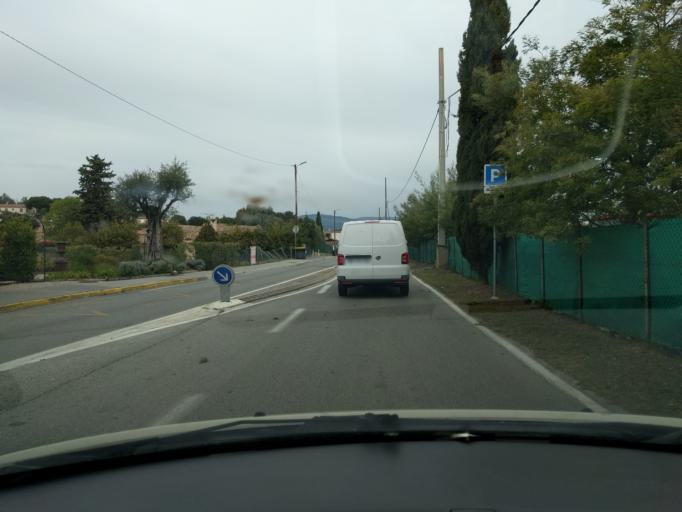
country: FR
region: Provence-Alpes-Cote d'Azur
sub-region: Departement des Alpes-Maritimes
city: La Roquette-sur-Siagne
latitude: 43.5951
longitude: 6.9564
